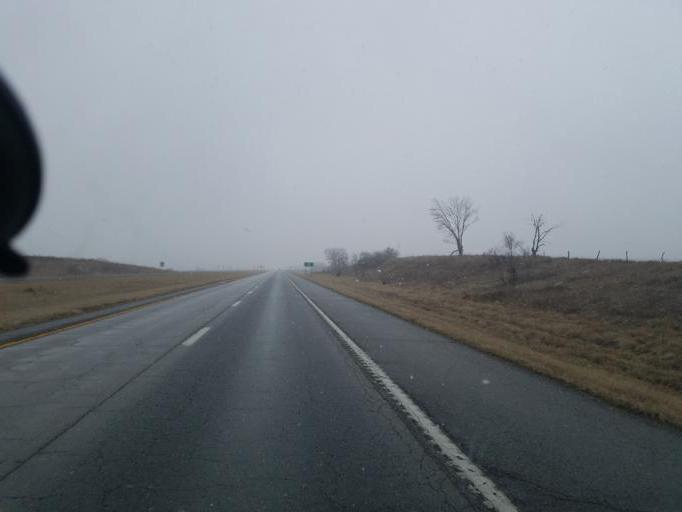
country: US
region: Missouri
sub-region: Macon County
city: La Plata
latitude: 39.9880
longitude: -92.4759
